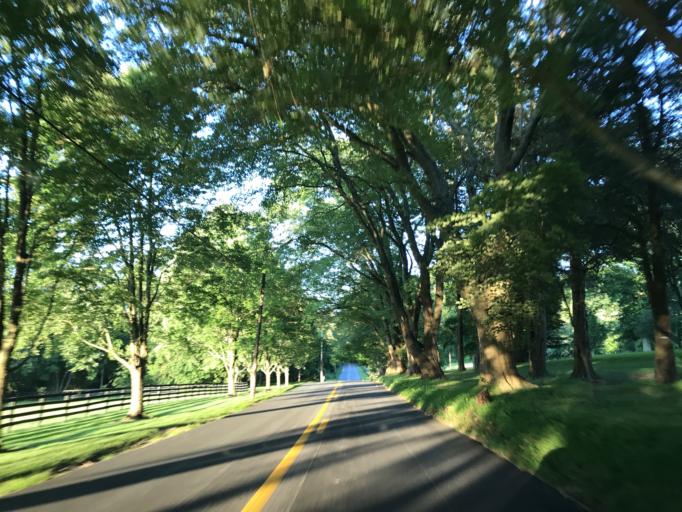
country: US
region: Maryland
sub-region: Baltimore County
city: Hunt Valley
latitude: 39.5633
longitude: -76.6983
